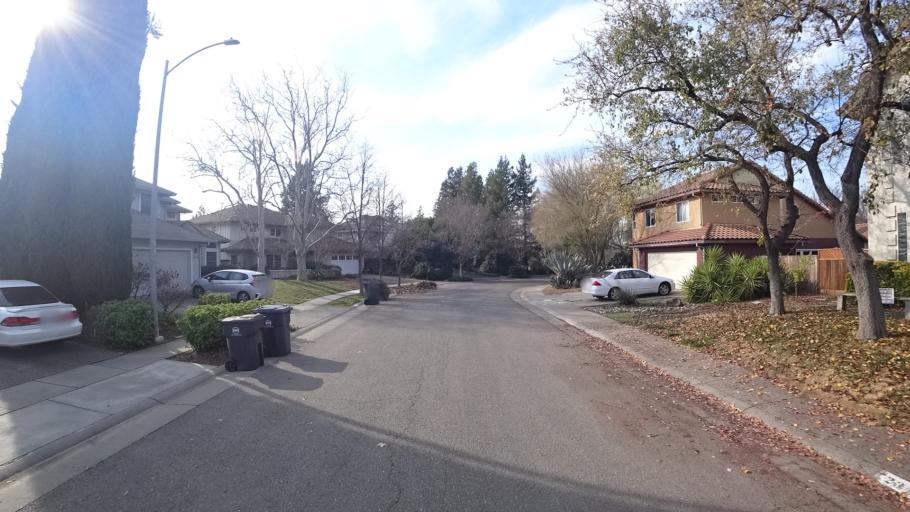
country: US
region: California
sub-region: Yolo County
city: Davis
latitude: 38.5587
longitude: -121.7814
